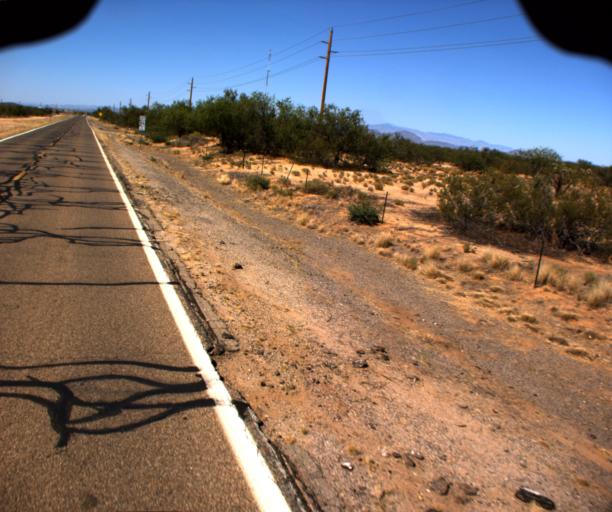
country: US
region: Arizona
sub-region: Pima County
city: Three Points
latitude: 32.0688
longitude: -111.3160
